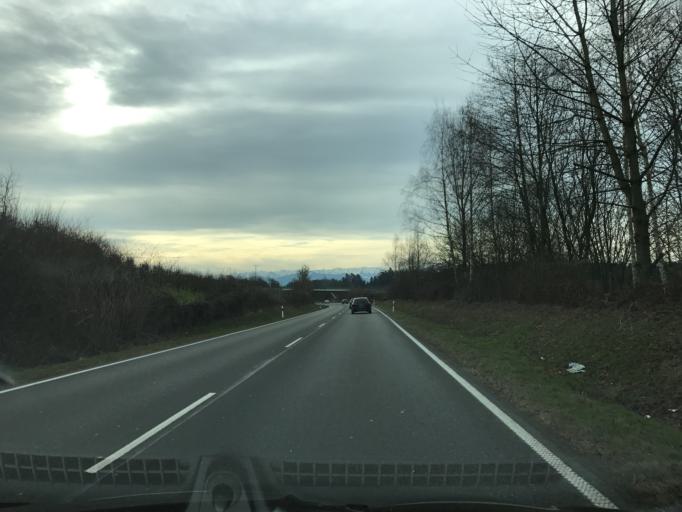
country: DE
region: Bavaria
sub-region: Swabia
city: Nonnenhorn
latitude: 47.5992
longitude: 9.6299
